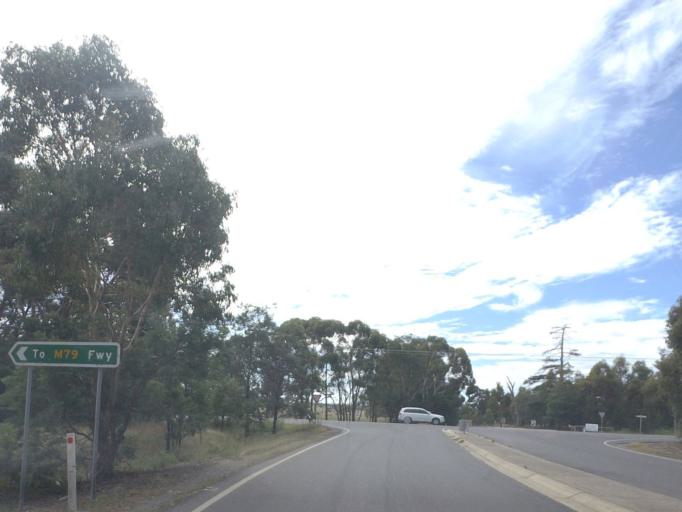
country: AU
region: Victoria
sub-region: Hume
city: Sunbury
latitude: -37.3511
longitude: 144.5550
